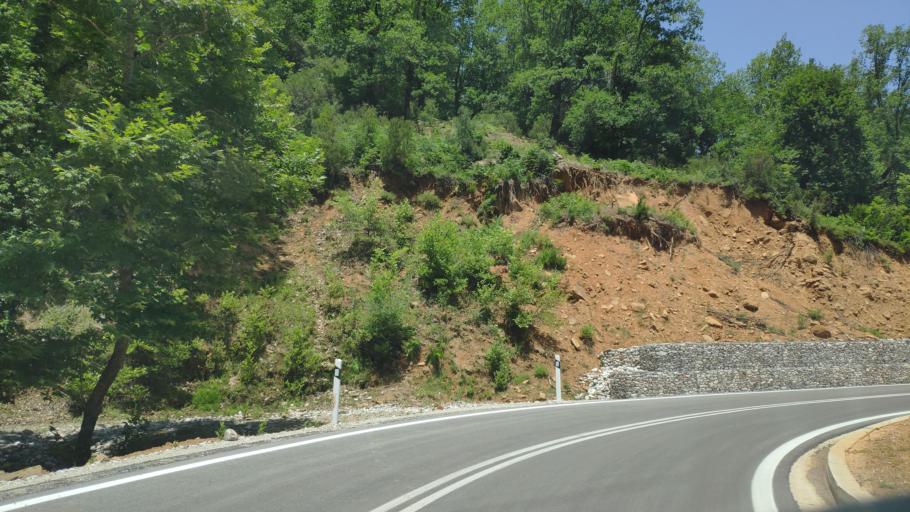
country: GR
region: Epirus
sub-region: Nomos Artas
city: Ano Kalentini
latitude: 39.1789
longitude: 21.3565
